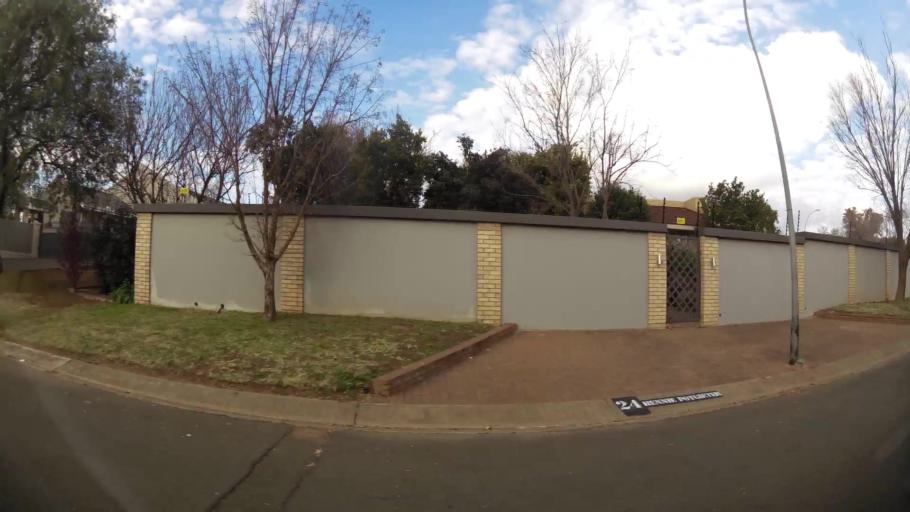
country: ZA
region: Orange Free State
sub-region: Mangaung Metropolitan Municipality
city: Bloemfontein
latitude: -29.0887
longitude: 26.1996
